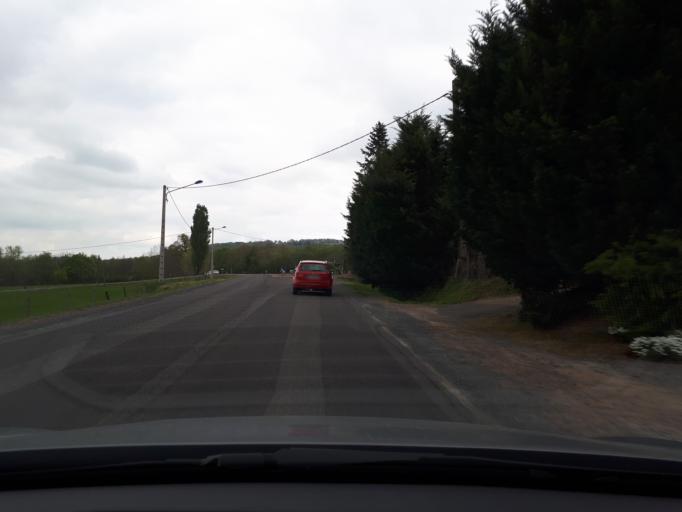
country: FR
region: Rhone-Alpes
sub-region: Departement de la Loire
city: Bellegarde-en-Forez
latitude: 45.6786
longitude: 4.2963
